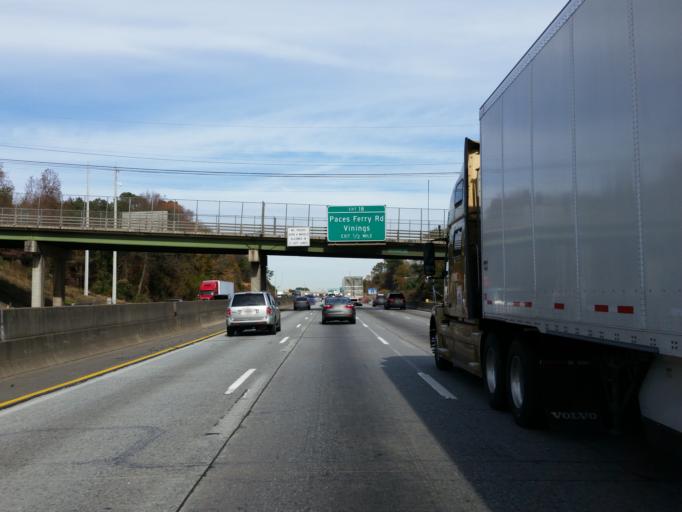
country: US
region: Georgia
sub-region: Cobb County
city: Vinings
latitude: 33.8544
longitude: -84.4835
